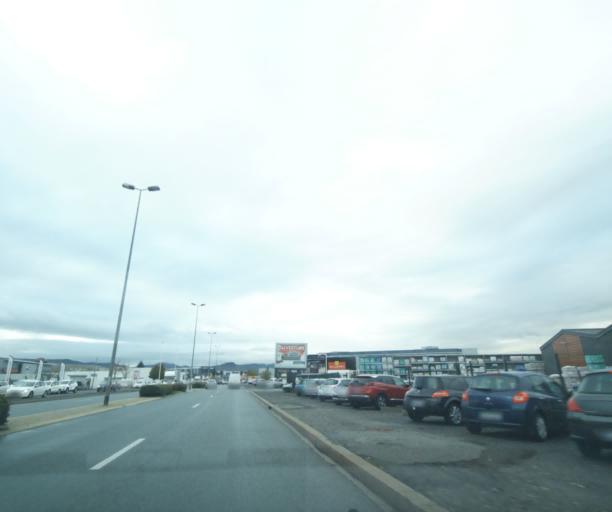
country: FR
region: Auvergne
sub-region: Departement du Puy-de-Dome
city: Aulnat
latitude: 45.7841
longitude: 3.1352
